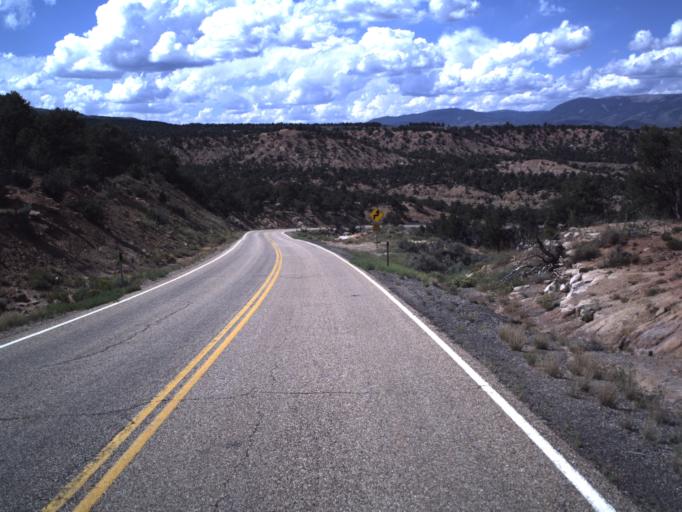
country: US
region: Utah
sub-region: Duchesne County
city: Duchesne
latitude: 40.3118
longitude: -110.6992
